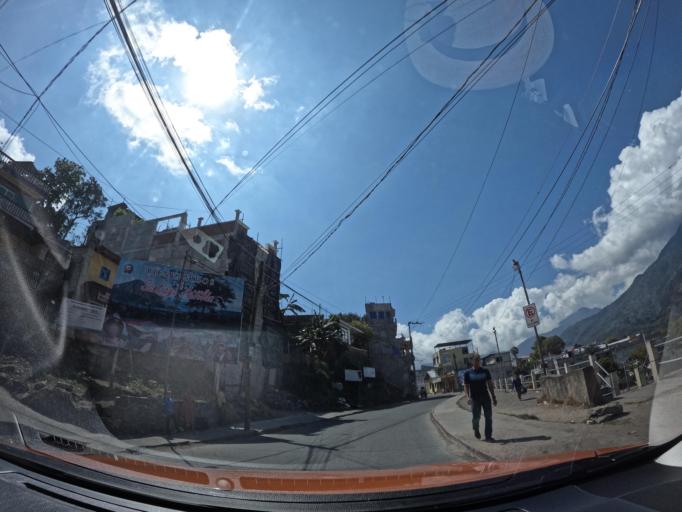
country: GT
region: Solola
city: Santiago Atitlan
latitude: 14.6427
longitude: -91.2279
